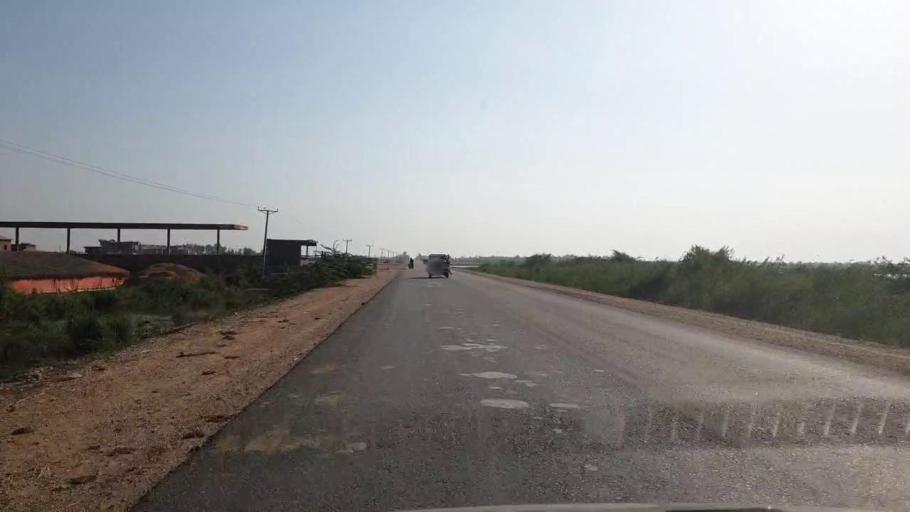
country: PK
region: Sindh
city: Badin
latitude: 24.6582
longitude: 68.9592
